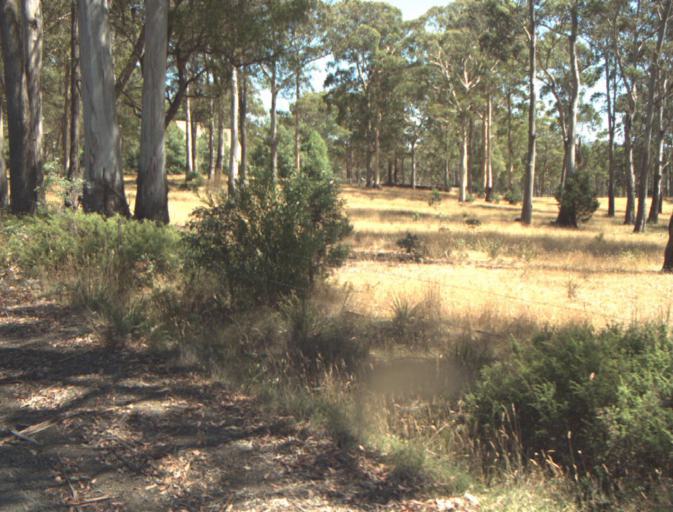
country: AU
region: Tasmania
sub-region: Launceston
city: Newstead
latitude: -41.3429
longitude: 147.3638
